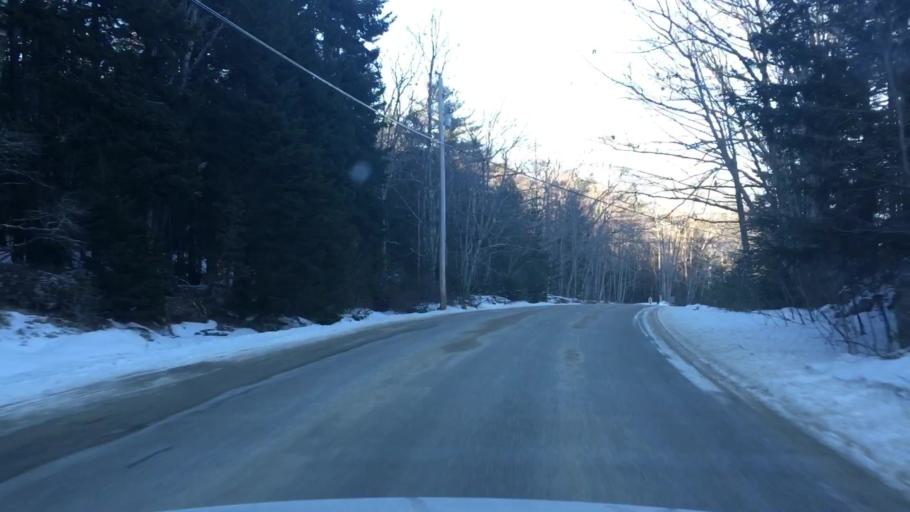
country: US
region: Maine
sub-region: Hancock County
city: Castine
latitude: 44.3554
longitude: -68.7786
